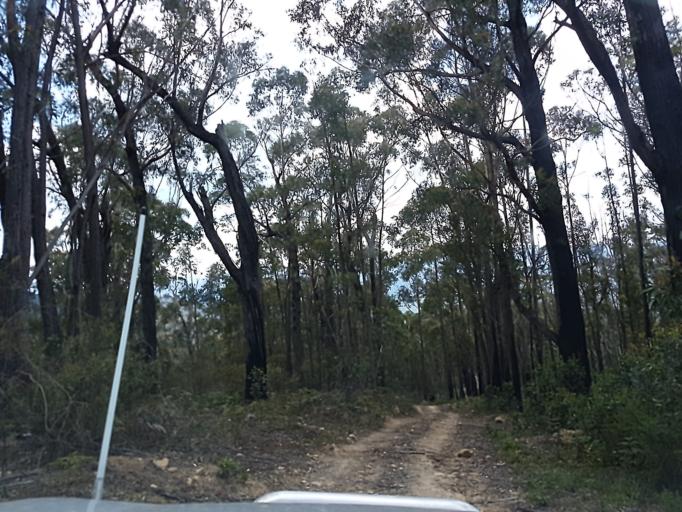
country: AU
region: Victoria
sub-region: East Gippsland
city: Lakes Entrance
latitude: -37.3466
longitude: 148.3351
